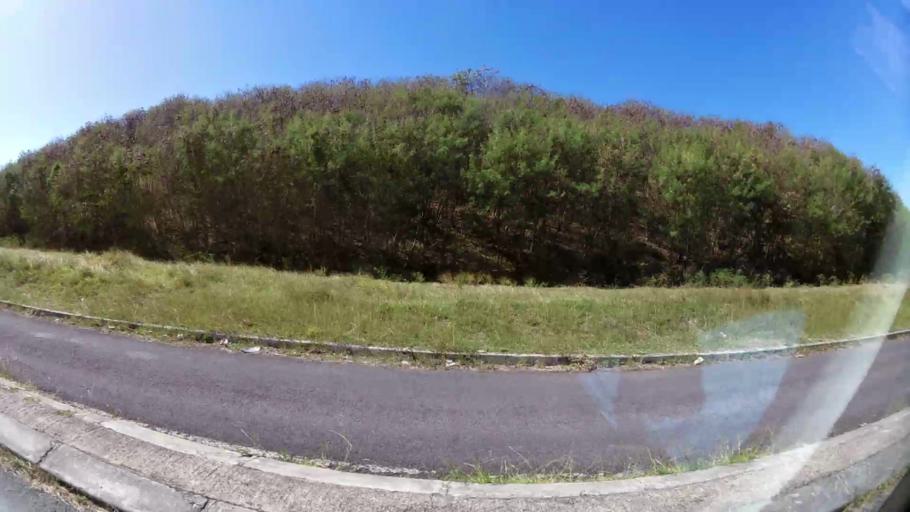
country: YT
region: Pamandzi
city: Pamandzi
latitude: -12.8045
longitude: 45.2832
